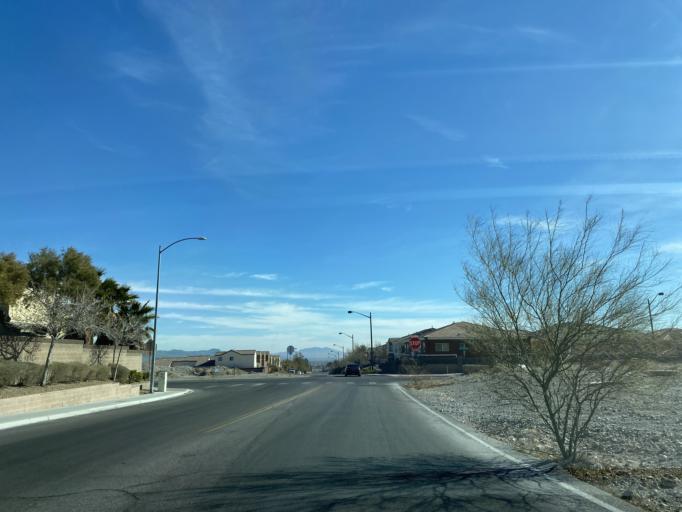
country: US
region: Nevada
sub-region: Clark County
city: Summerlin South
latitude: 36.3029
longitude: -115.3020
